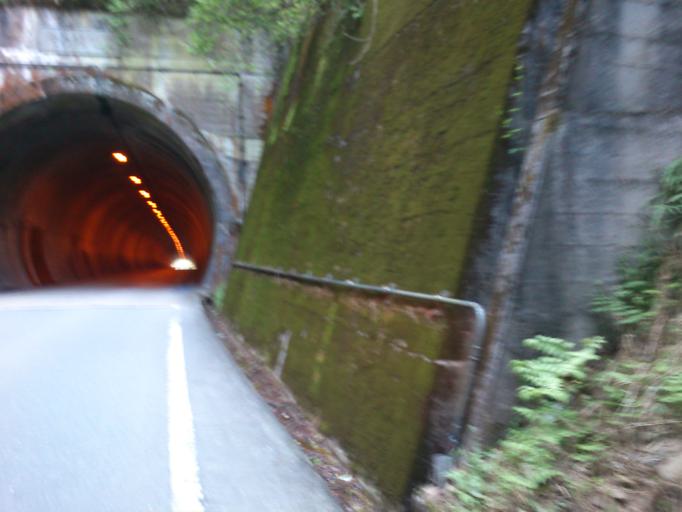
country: JP
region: Kyoto
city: Fukuchiyama
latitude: 35.2547
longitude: 135.0596
